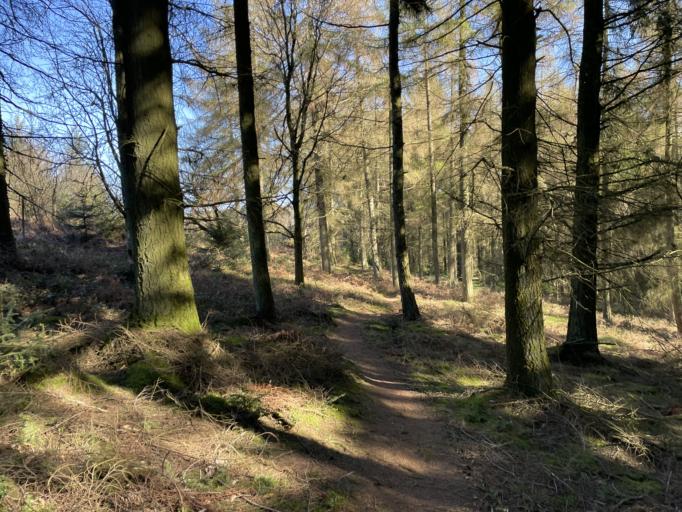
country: GB
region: England
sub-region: Somerset
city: Minehead
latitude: 51.1678
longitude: -3.4469
